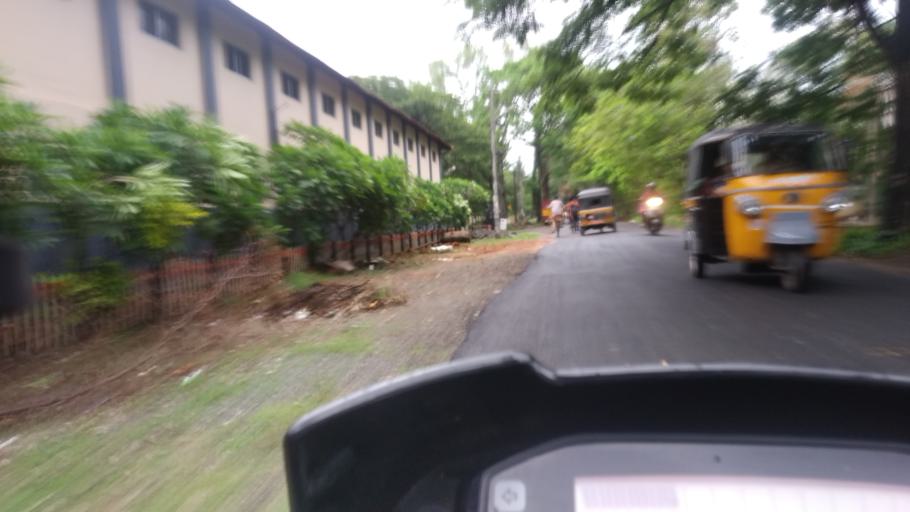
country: IN
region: Kerala
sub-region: Alappuzha
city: Alleppey
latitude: 9.5001
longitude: 76.3262
